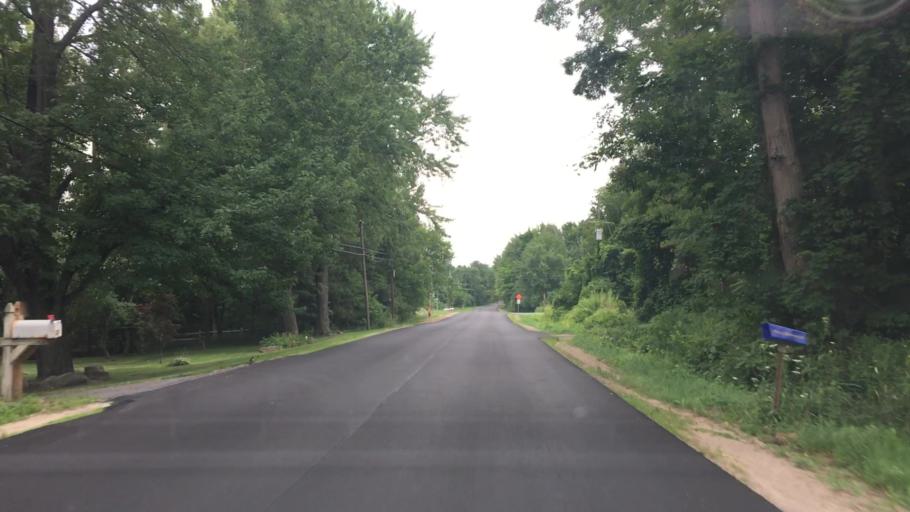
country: US
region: New York
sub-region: Clinton County
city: Peru
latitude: 44.5643
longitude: -73.5687
